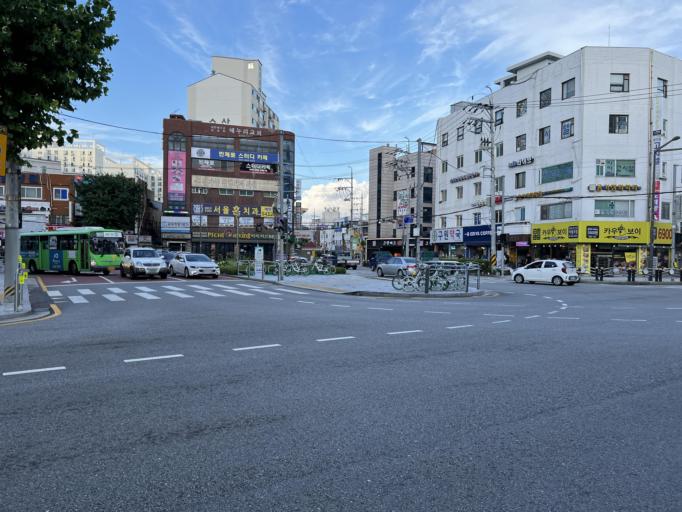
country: KR
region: Seoul
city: Seoul
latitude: 37.6039
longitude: 127.0370
